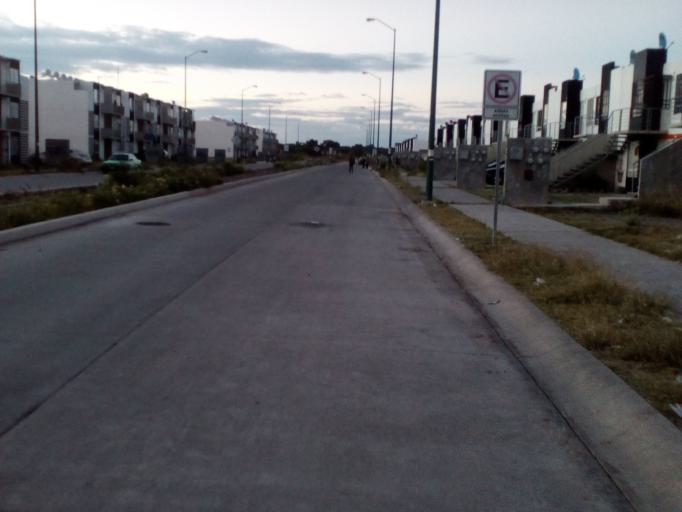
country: MX
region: Guanajuato
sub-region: Leon
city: Fraccionamiento Paseo de las Torres
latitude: 21.1880
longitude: -101.7666
